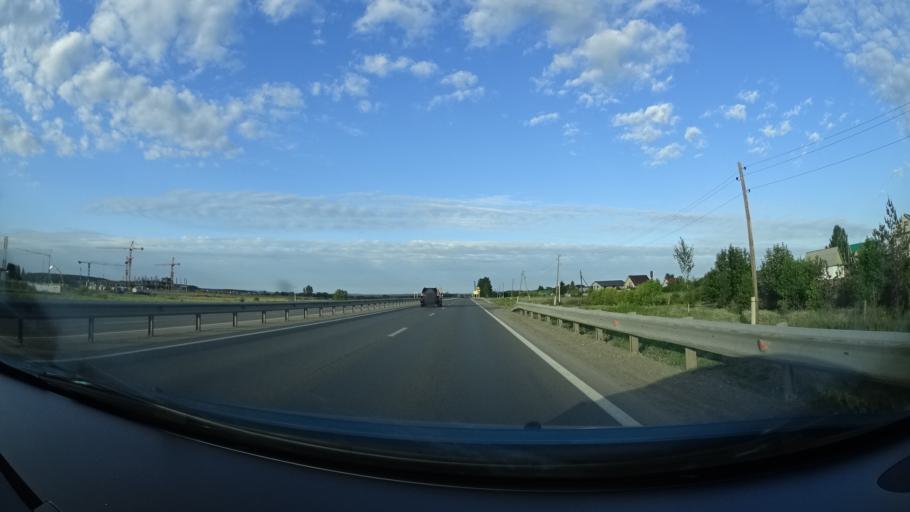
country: RU
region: Perm
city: Kultayevo
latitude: 57.9213
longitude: 56.0090
